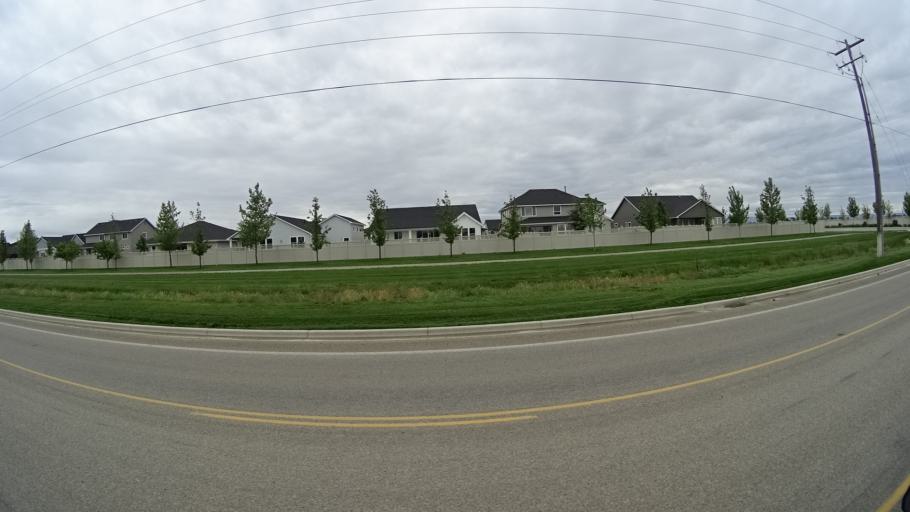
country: US
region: Idaho
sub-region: Ada County
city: Meridian
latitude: 43.6485
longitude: -116.4397
